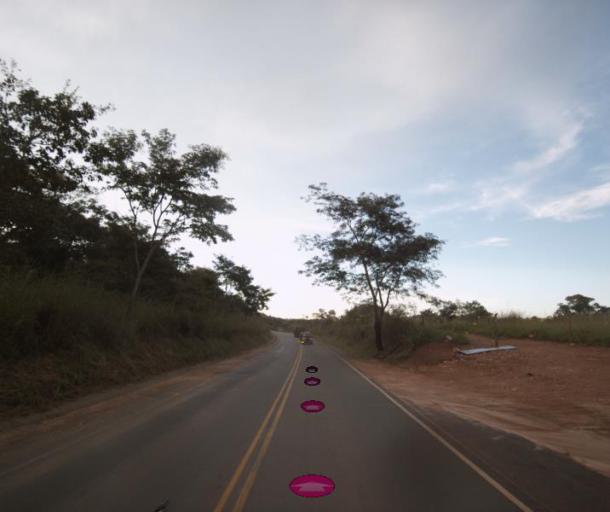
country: BR
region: Goias
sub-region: Anapolis
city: Anapolis
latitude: -16.1449
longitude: -48.8906
